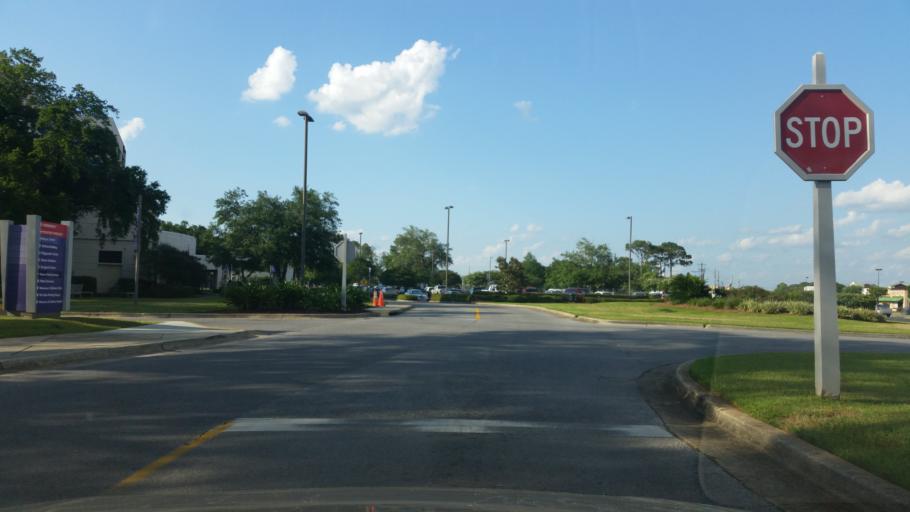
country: US
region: Florida
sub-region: Escambia County
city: Brent
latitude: 30.4757
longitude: -87.2113
